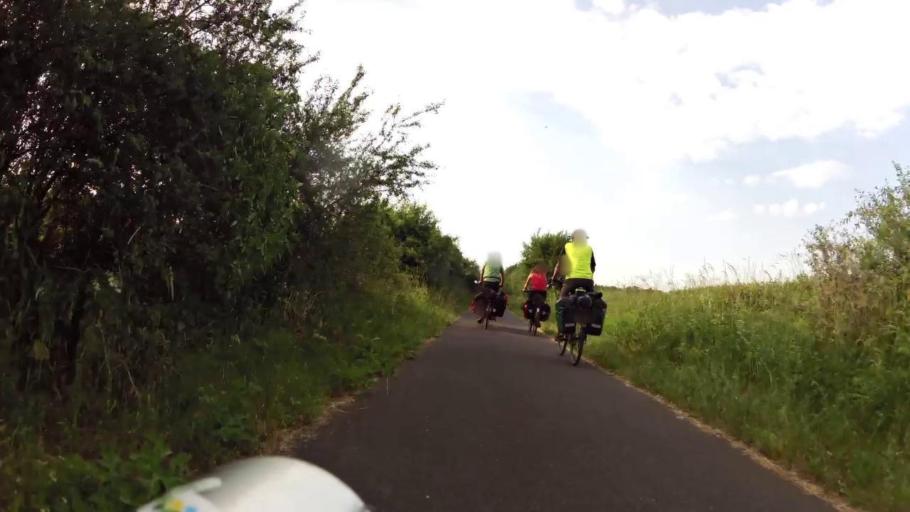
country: PL
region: Kujawsko-Pomorskie
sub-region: Powiat torunski
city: Lubianka
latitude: 53.1392
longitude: 18.4599
